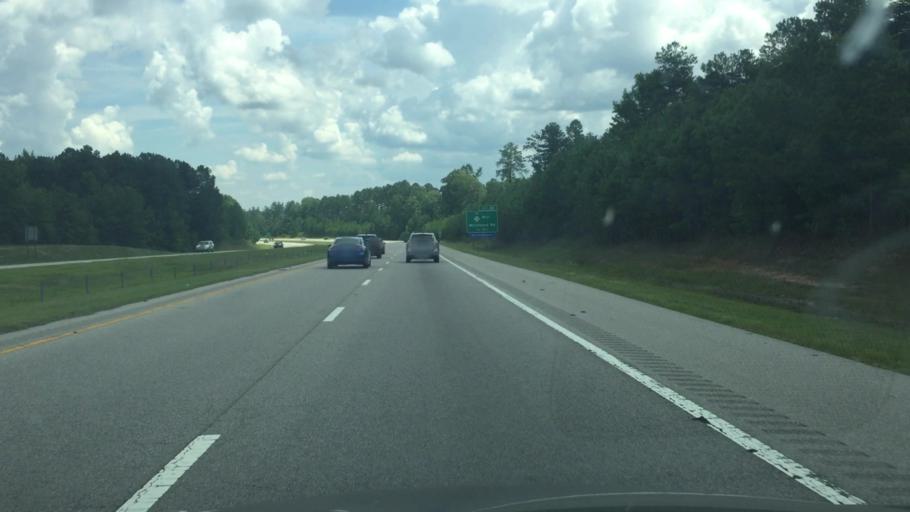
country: US
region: North Carolina
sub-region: Richmond County
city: Ellerbe
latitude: 35.0601
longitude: -79.7447
